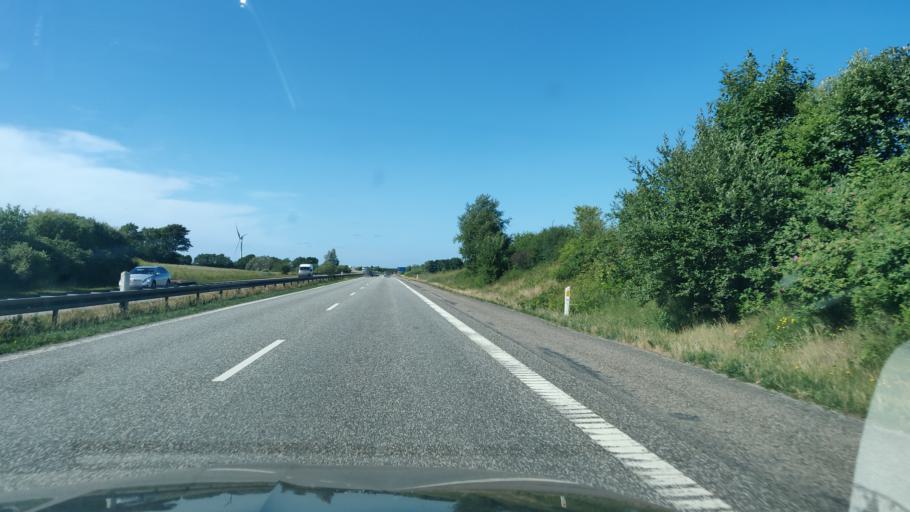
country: DK
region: North Denmark
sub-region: Mariagerfjord Kommune
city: Hobro
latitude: 56.6590
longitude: 9.7362
